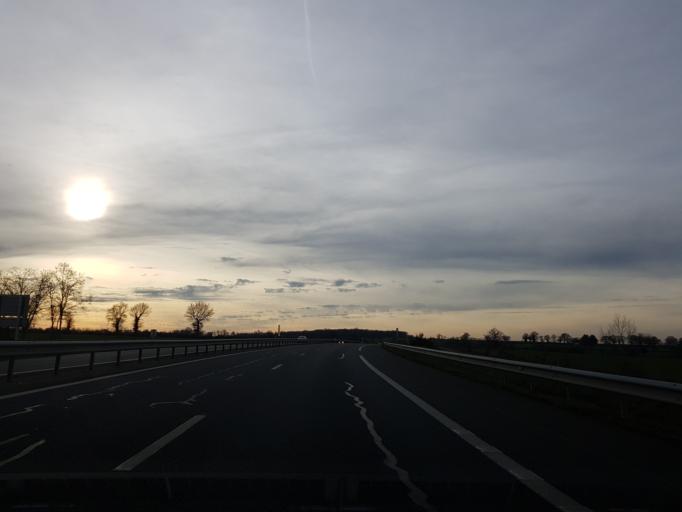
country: FR
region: Auvergne
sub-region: Departement de l'Allier
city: Desertines
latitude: 46.3770
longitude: 2.6775
